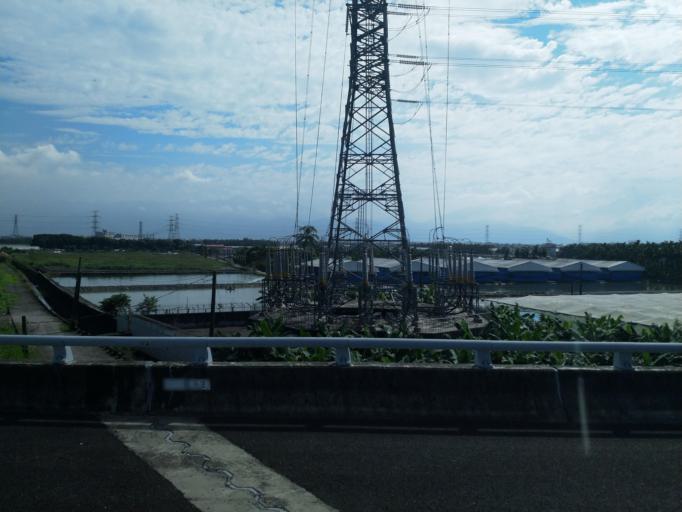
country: TW
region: Taiwan
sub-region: Pingtung
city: Pingtung
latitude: 22.8166
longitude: 120.4867
